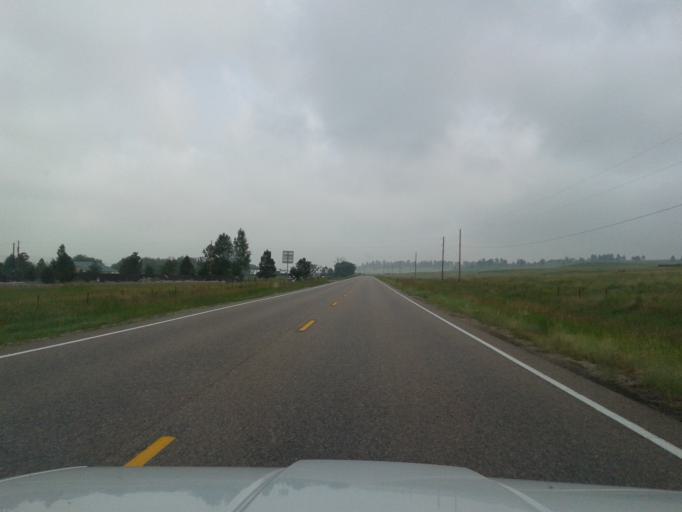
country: US
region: Colorado
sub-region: Elbert County
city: Elizabeth
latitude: 39.2394
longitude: -104.6965
